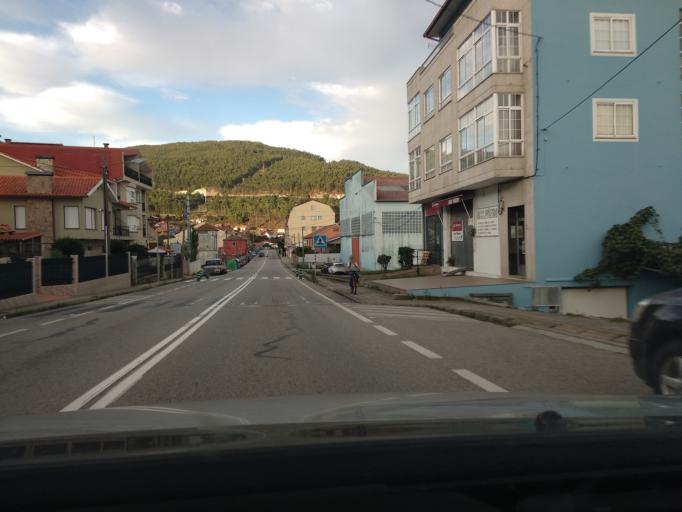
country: ES
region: Galicia
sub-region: Provincia de Pontevedra
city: Vigo
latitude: 42.2876
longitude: -8.6809
